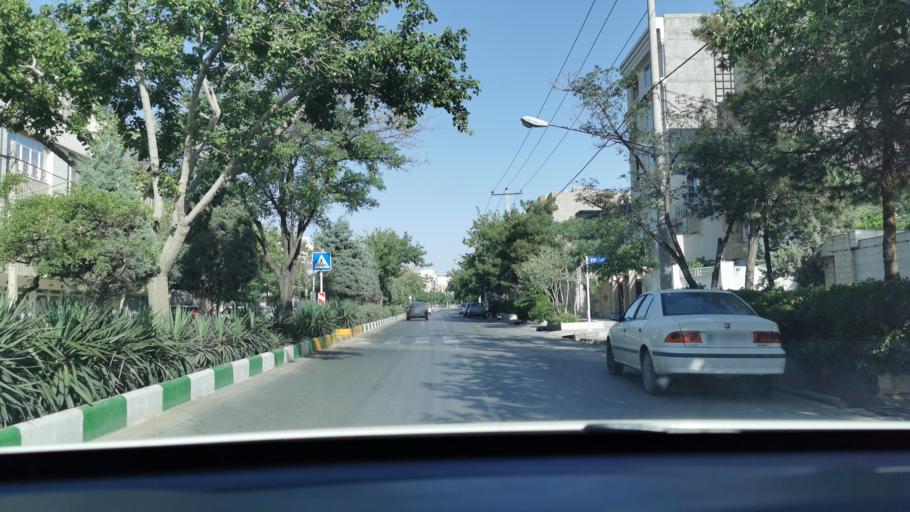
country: IR
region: Razavi Khorasan
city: Mashhad
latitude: 36.3380
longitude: 59.5106
